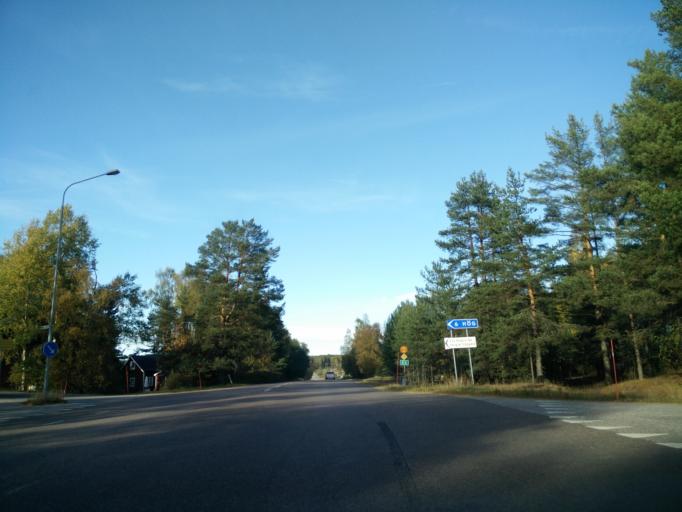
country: SE
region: Gaevleborg
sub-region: Hudiksvalls Kommun
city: Hudiksvall
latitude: 61.7530
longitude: 17.1206
